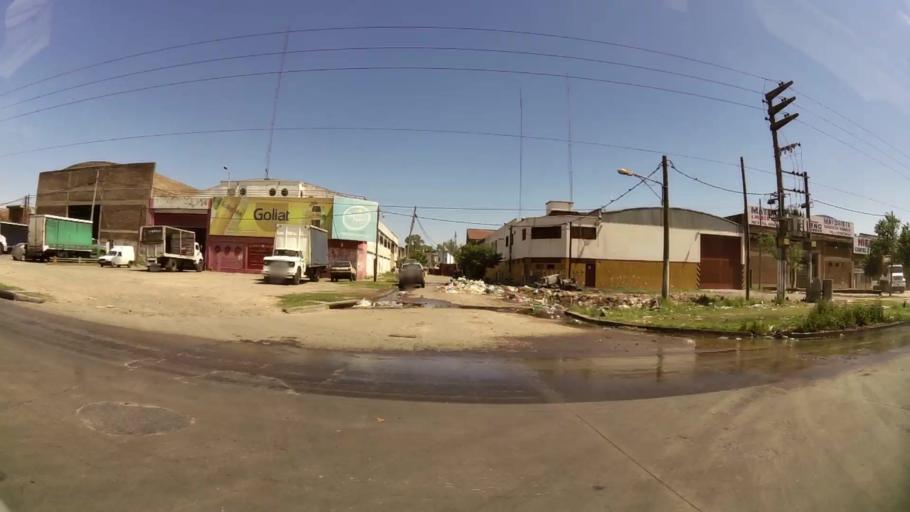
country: AR
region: Buenos Aires
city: Caseros
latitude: -34.5634
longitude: -58.5764
